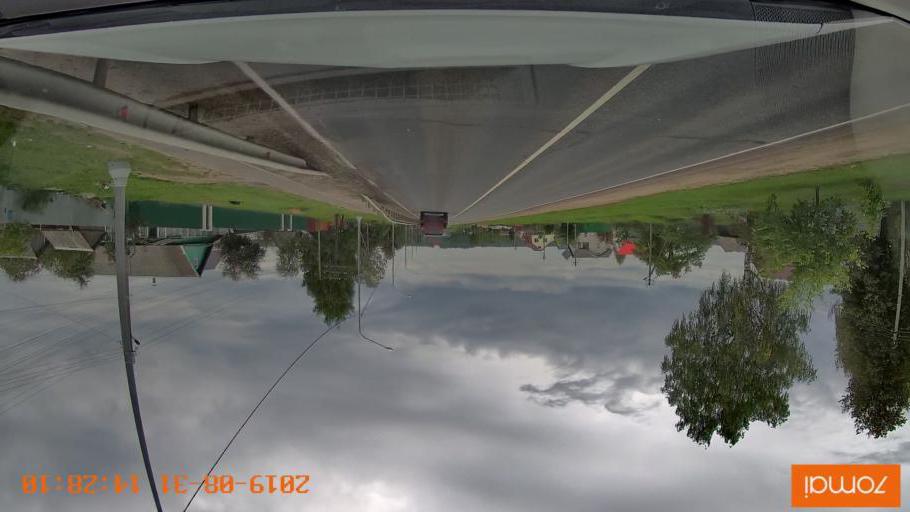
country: RU
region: Smolensk
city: Yekimovichi
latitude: 54.1192
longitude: 33.3096
